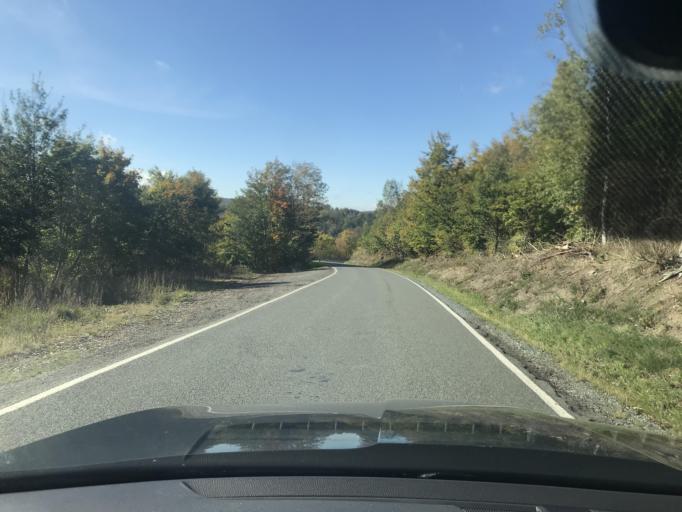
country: DE
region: Saxony-Anhalt
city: Timmenrode
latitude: 51.7304
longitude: 10.9764
